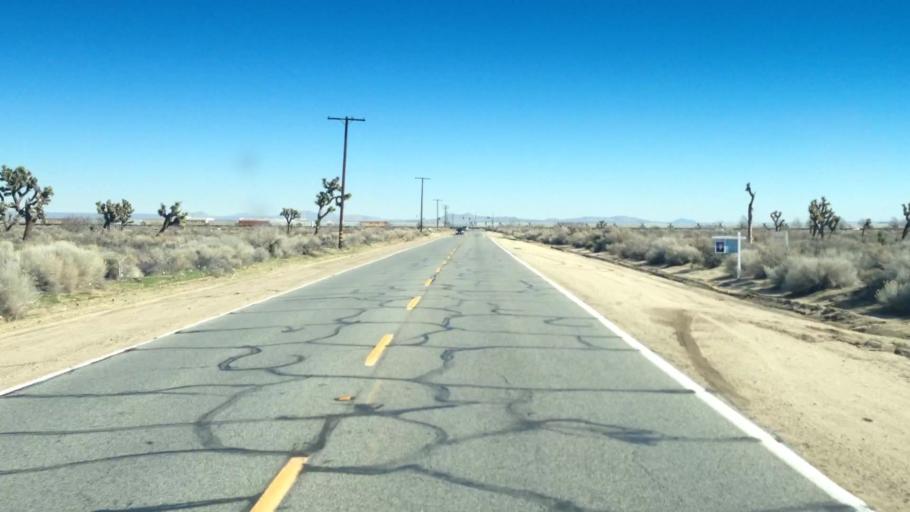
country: US
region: California
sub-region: Los Angeles County
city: Desert View Highlands
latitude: 34.6311
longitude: -118.1320
